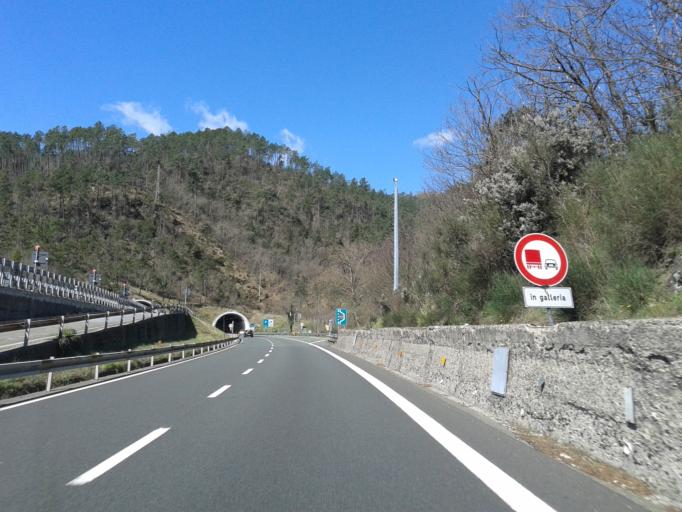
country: IT
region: Liguria
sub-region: Provincia di La Spezia
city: Framura
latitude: 44.2390
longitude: 9.5954
